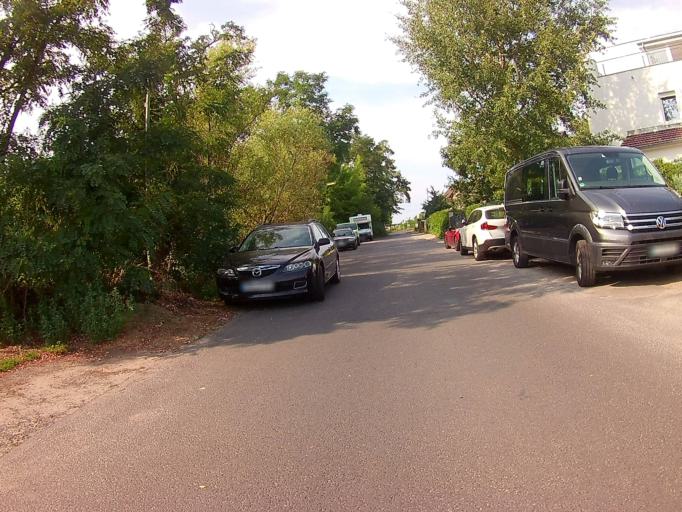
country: DE
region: Berlin
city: Grunau
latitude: 52.4269
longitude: 13.5723
